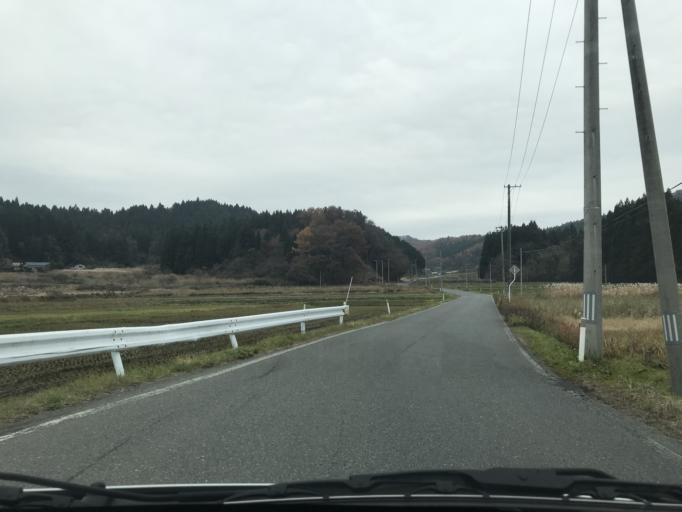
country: JP
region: Iwate
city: Kitakami
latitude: 39.2785
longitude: 141.1737
